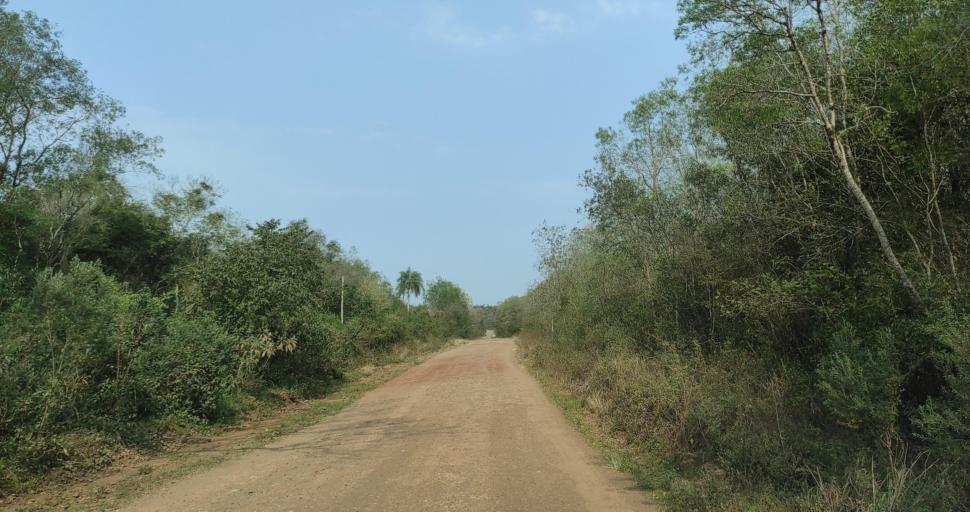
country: AR
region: Misiones
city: Cerro Cora
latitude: -27.5250
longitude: -55.5972
